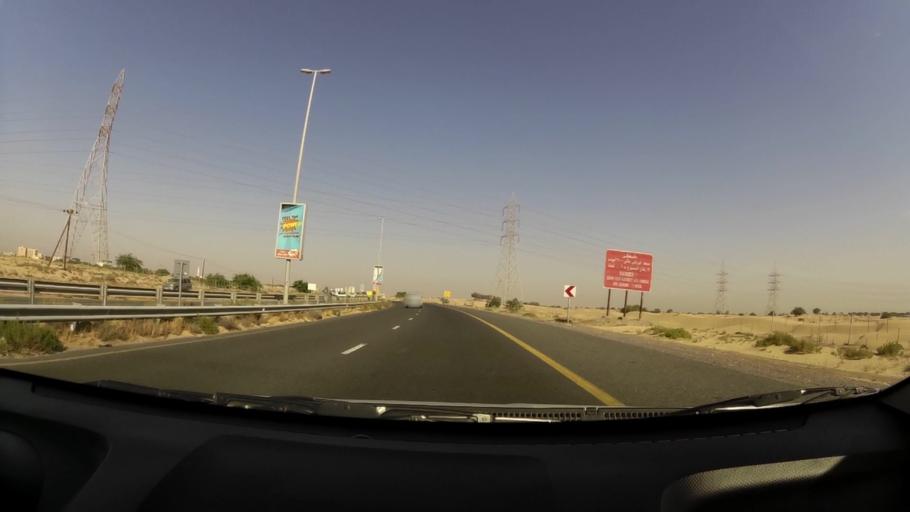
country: AE
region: Umm al Qaywayn
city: Umm al Qaywayn
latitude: 25.4715
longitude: 55.5789
